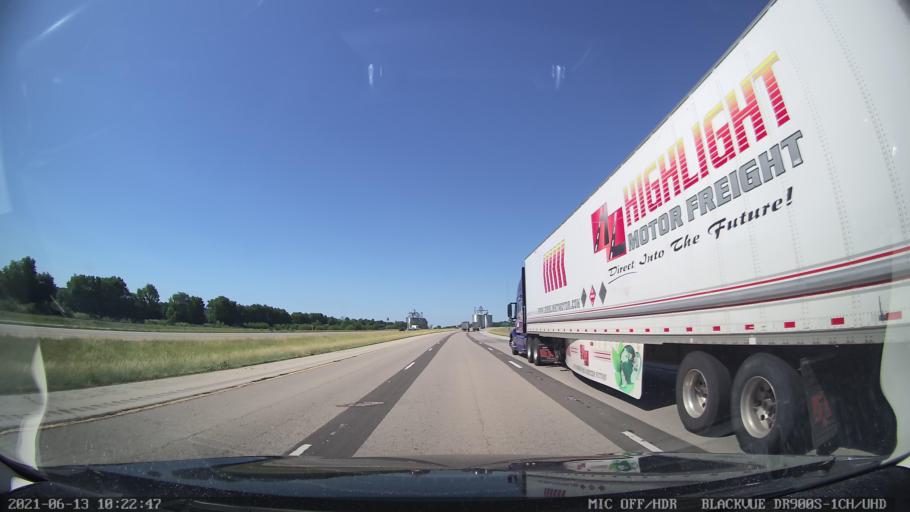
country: US
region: Illinois
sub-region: Sangamon County
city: Williamsville
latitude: 40.0325
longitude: -89.4746
